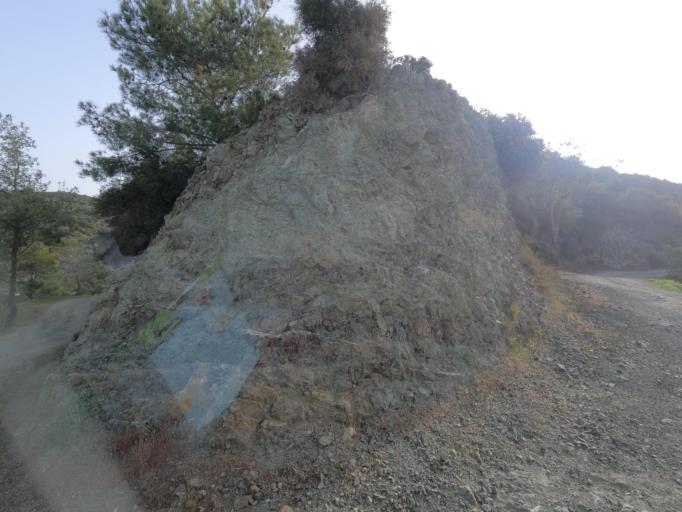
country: CY
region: Pafos
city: Polis
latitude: 35.0008
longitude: 32.3393
